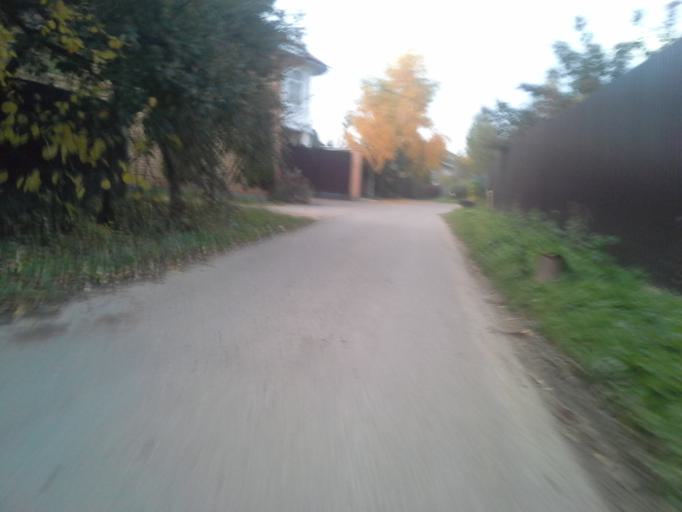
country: RU
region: Moskovskaya
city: Kommunarka
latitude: 55.5069
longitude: 37.4381
